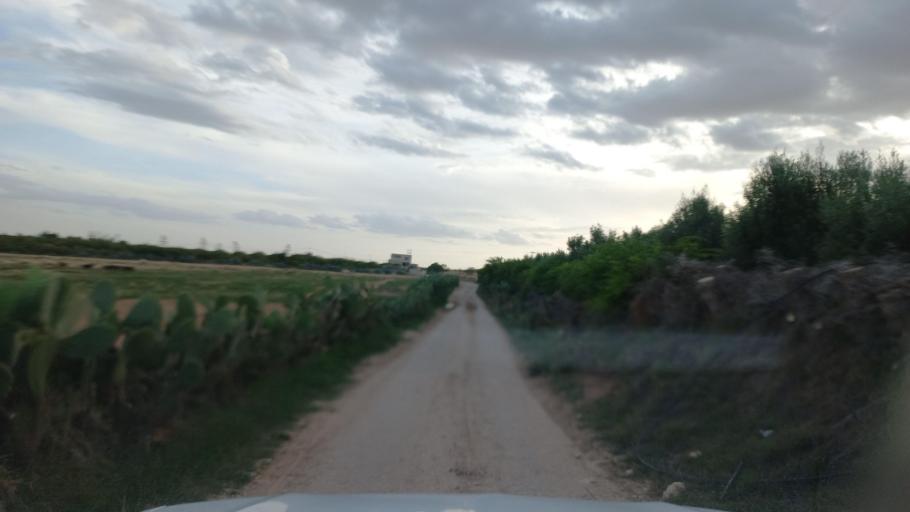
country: TN
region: Al Qasrayn
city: Sbiba
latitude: 35.4280
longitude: 9.0979
